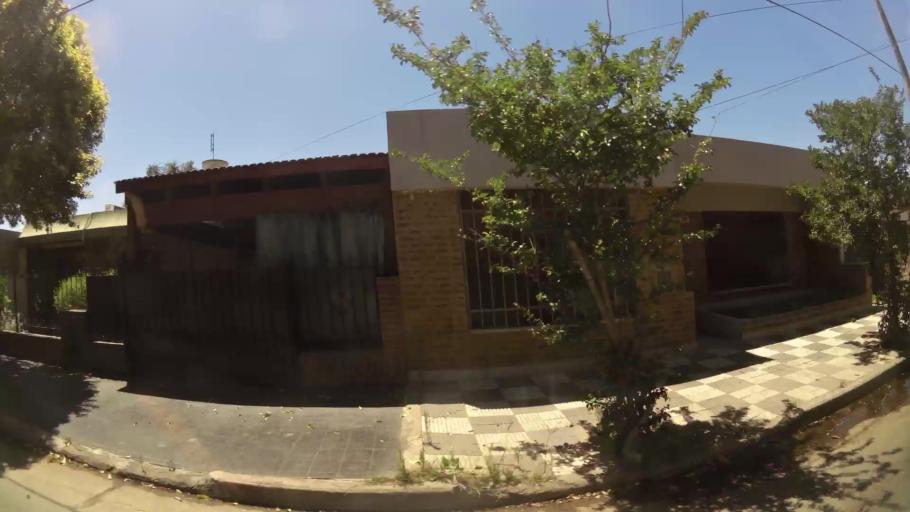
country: AR
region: Cordoba
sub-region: Departamento de Capital
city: Cordoba
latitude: -31.4294
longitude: -64.1272
